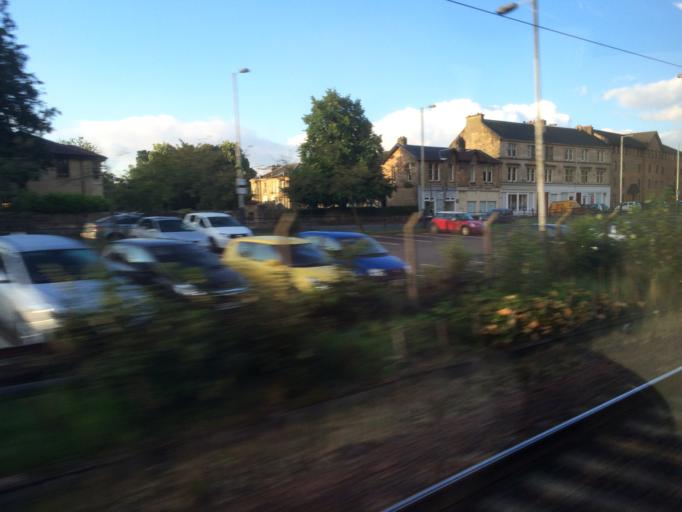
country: GB
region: Scotland
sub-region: East Dunbartonshire
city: Kirkintilloch
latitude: 55.9208
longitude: -4.1560
